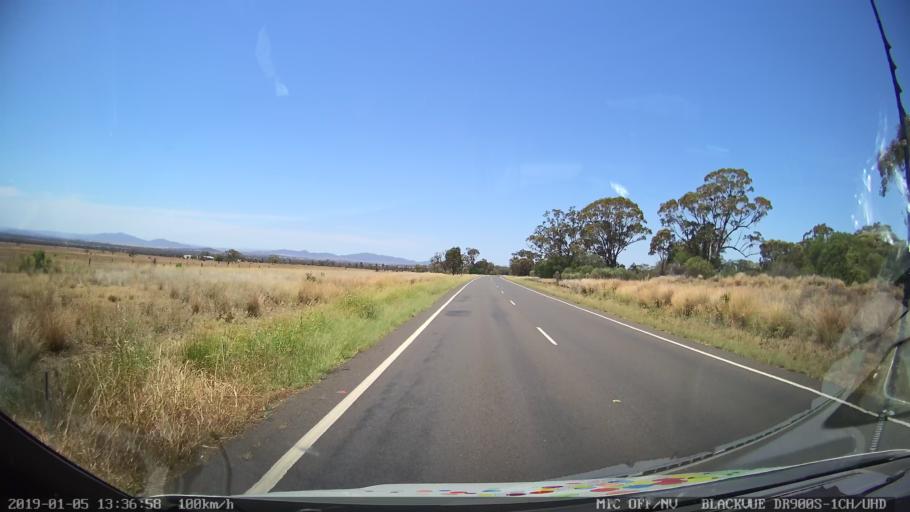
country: AU
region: New South Wales
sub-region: Gunnedah
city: Gunnedah
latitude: -30.9825
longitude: 150.1733
